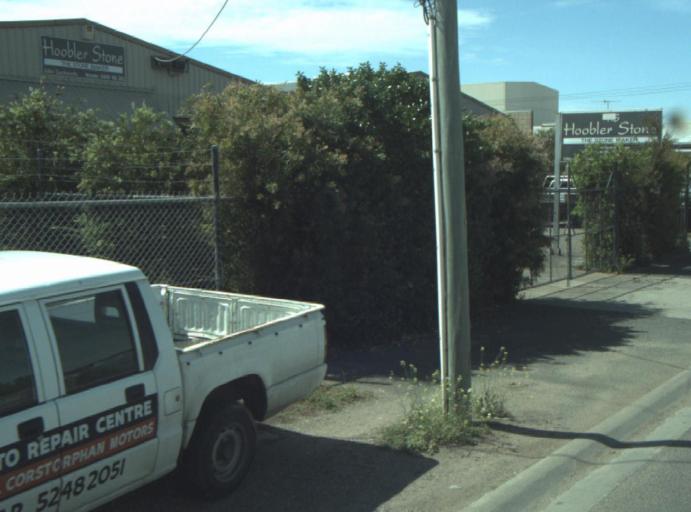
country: AU
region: Victoria
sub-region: Greater Geelong
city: East Geelong
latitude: -38.1650
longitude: 144.4093
